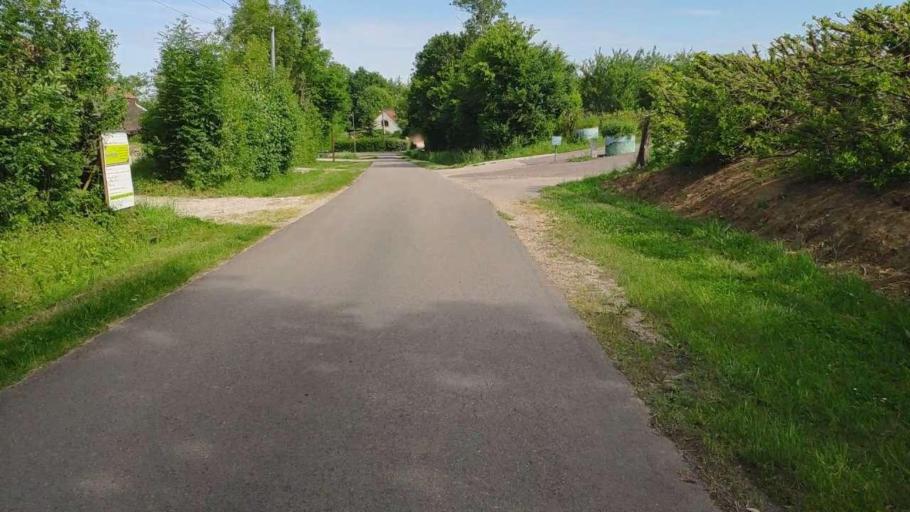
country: FR
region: Franche-Comte
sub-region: Departement du Jura
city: Bletterans
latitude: 46.7148
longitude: 5.4637
